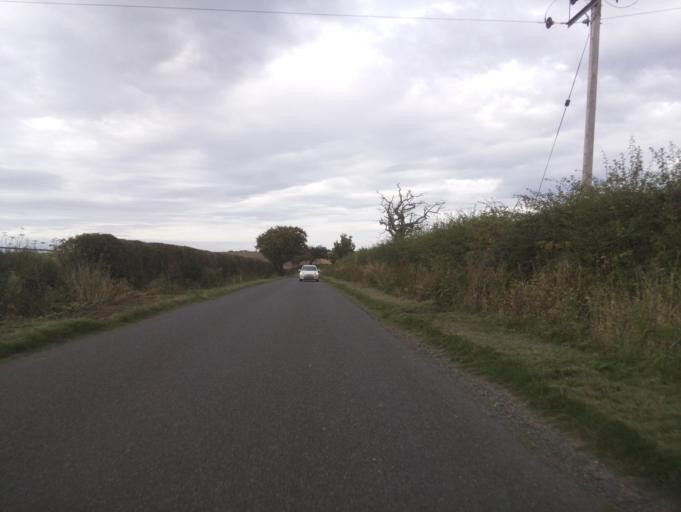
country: GB
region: Scotland
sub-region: Fife
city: Saint Andrews
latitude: 56.3031
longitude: -2.7864
